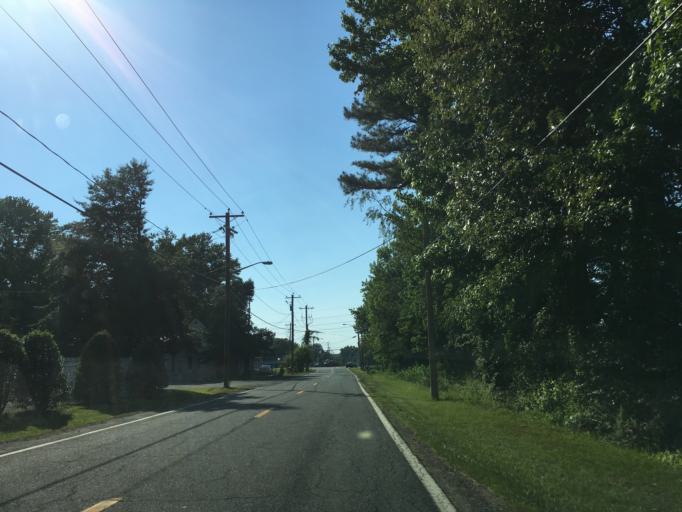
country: US
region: Maryland
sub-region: Queen Anne's County
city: Grasonville
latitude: 38.9866
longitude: -76.1509
